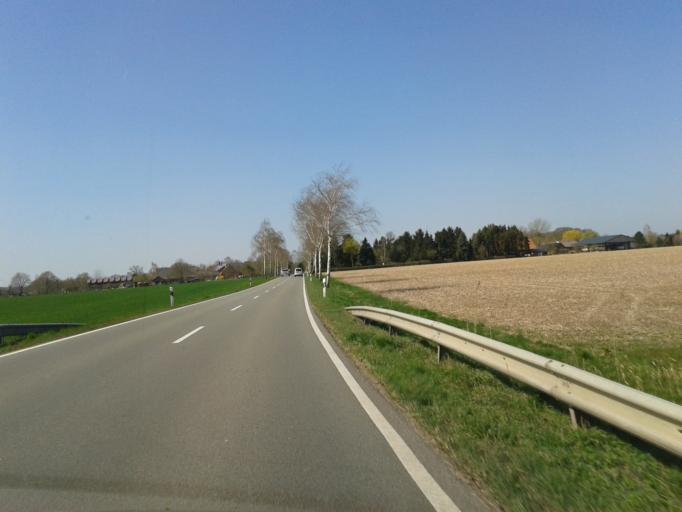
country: DE
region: Lower Saxony
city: Wustrow
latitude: 52.9382
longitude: 11.1048
